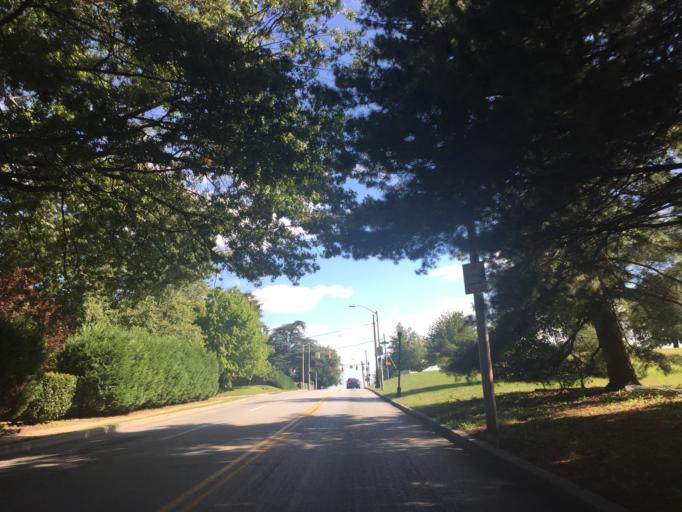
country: US
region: Maryland
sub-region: City of Baltimore
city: Baltimore
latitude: 39.3254
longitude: -76.5796
